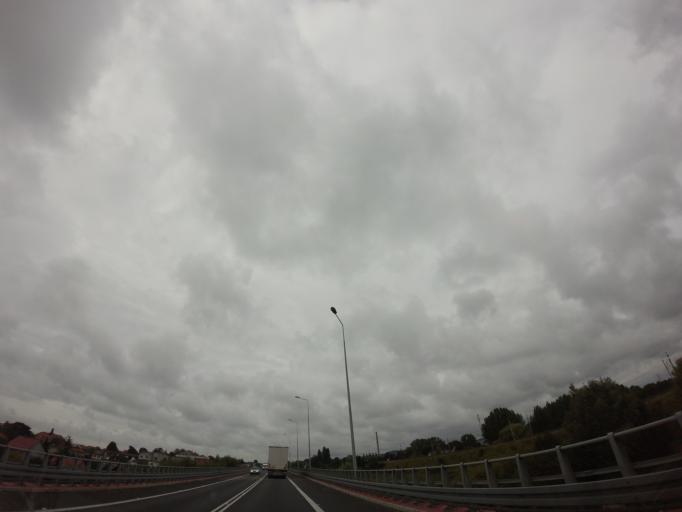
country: PL
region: West Pomeranian Voivodeship
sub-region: Powiat kamienski
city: Wolin
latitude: 53.8474
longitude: 14.6155
